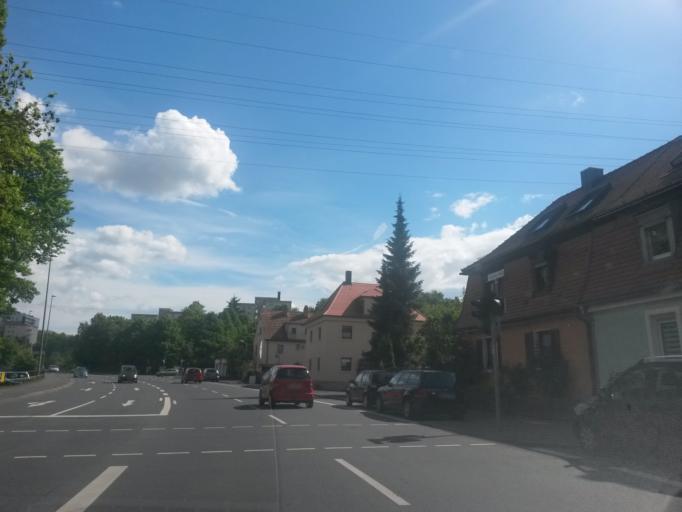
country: DE
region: Bavaria
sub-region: Regierungsbezirk Unterfranken
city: Wuerzburg
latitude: 49.8147
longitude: 9.9621
